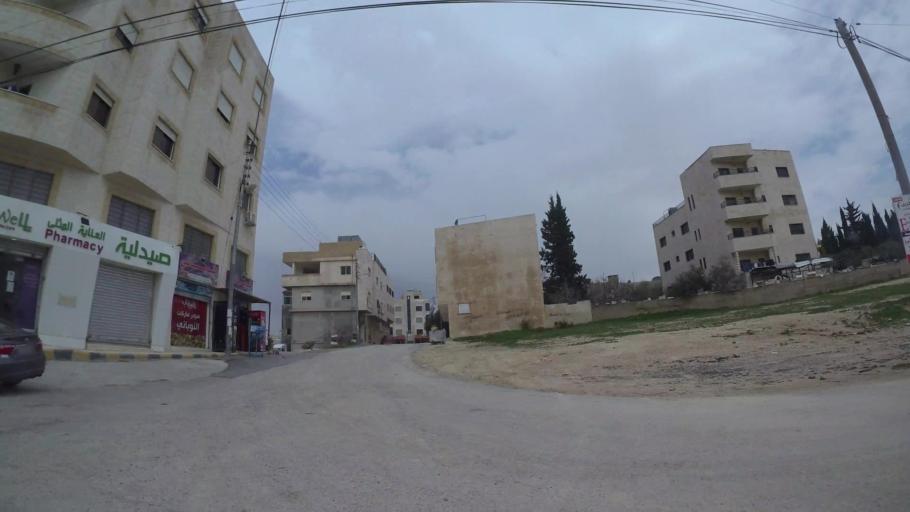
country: JO
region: Amman
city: Umm as Summaq
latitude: 31.9055
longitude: 35.8413
